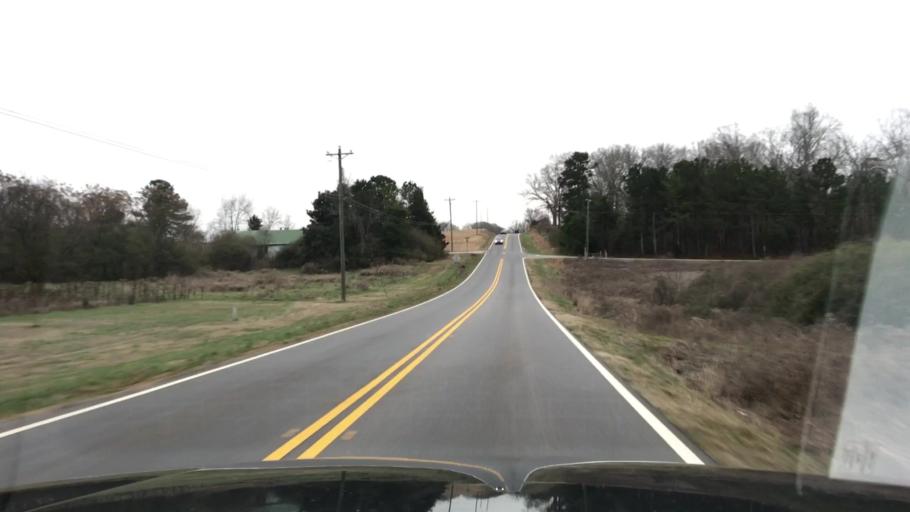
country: US
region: Georgia
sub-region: Walton County
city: Monroe
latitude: 33.8874
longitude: -83.7795
